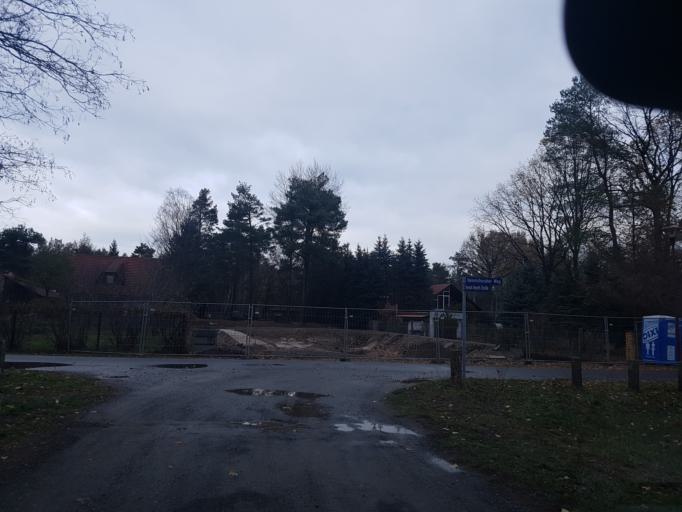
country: DE
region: Brandenburg
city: Finsterwalde
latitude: 51.6412
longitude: 13.6761
